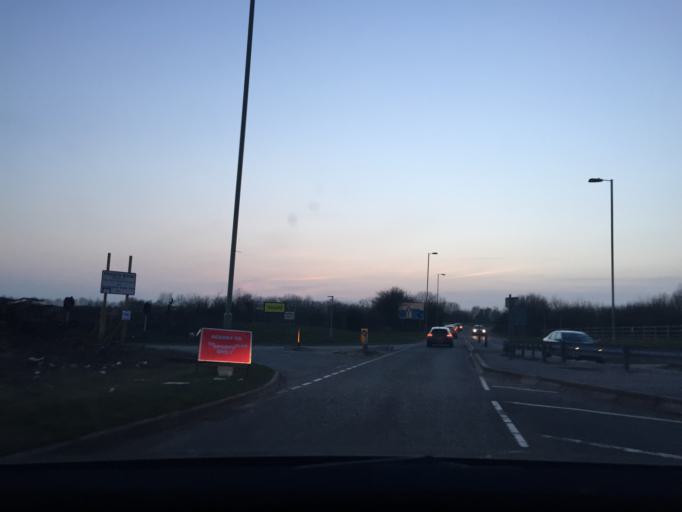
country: GB
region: England
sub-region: Hampshire
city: Totton
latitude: 50.9336
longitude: -1.4697
